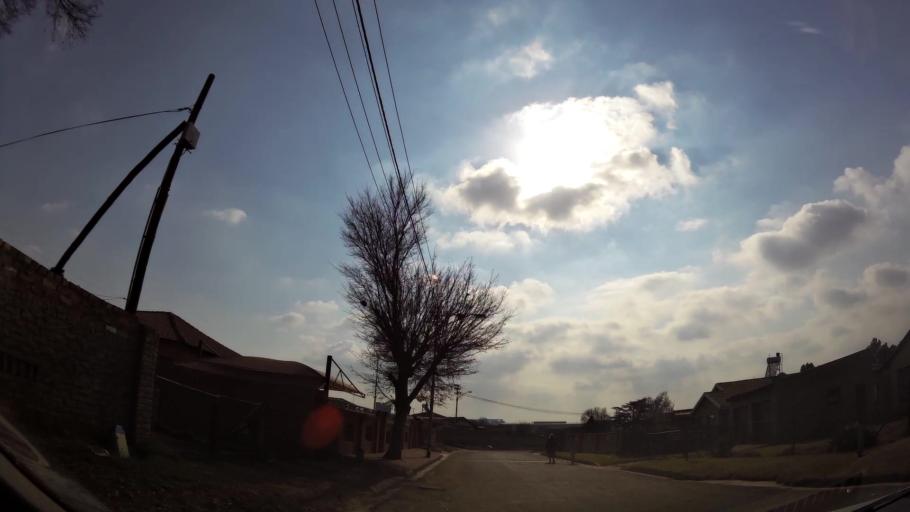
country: ZA
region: Gauteng
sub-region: City of Johannesburg Metropolitan Municipality
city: Modderfontein
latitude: -26.1563
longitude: 28.2034
